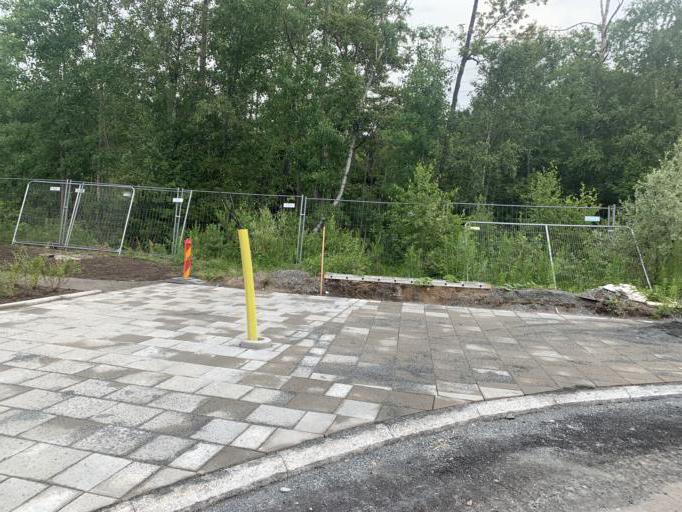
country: SE
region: Stockholm
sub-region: Solna Kommun
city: Rasunda
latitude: 59.3866
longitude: 17.9880
